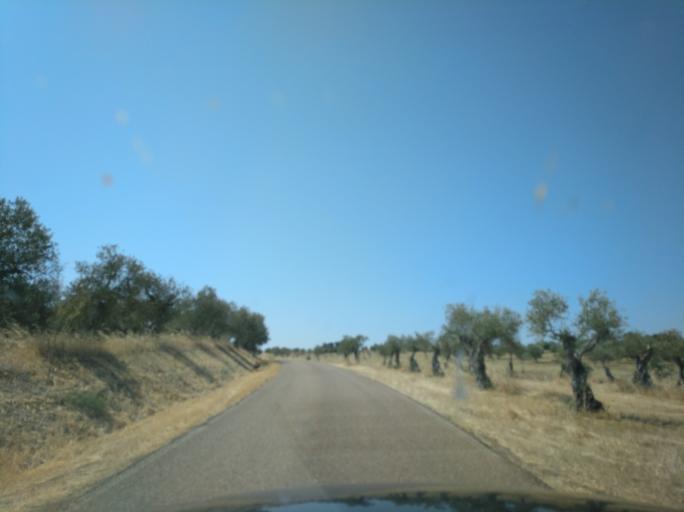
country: PT
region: Portalegre
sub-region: Campo Maior
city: Campo Maior
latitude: 39.0414
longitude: -7.0292
